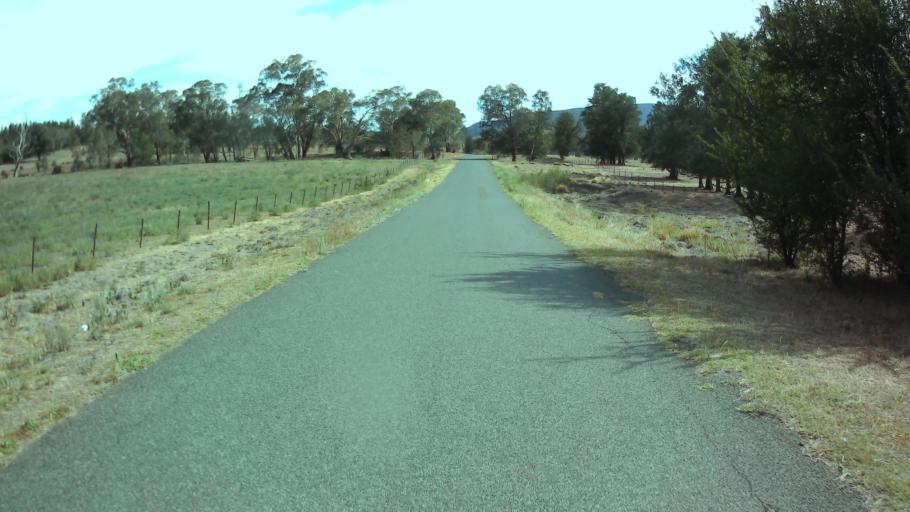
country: AU
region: New South Wales
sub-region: Weddin
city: Grenfell
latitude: -33.8130
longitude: 148.2923
